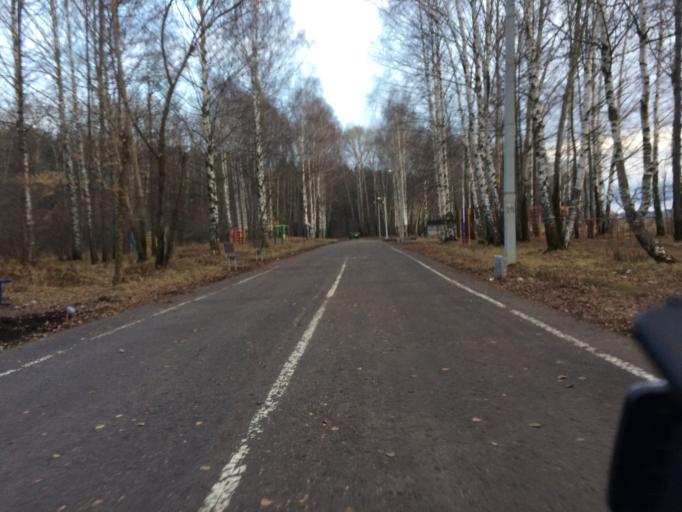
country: RU
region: Mariy-El
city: Yoshkar-Ola
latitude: 56.6230
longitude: 47.9155
